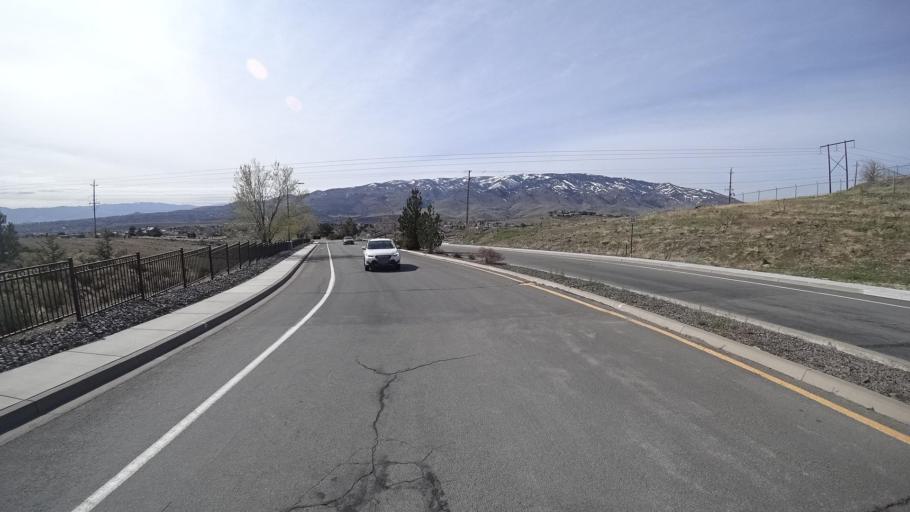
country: US
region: Nevada
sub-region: Washoe County
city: Mogul
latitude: 39.5333
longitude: -119.9001
